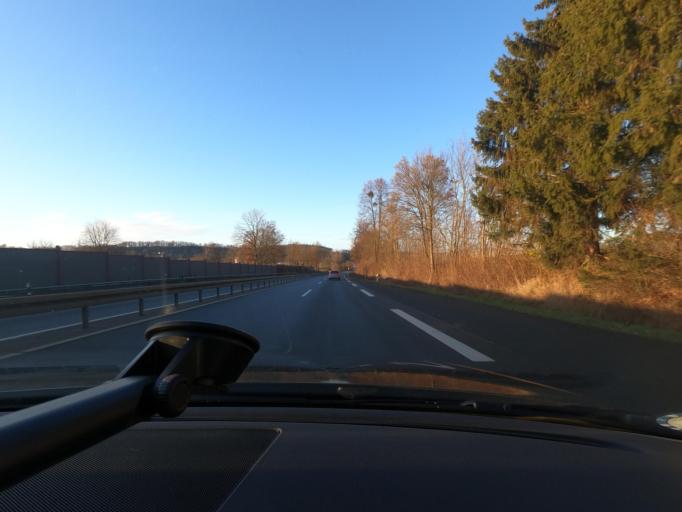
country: DE
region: Lower Saxony
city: Badenhausen
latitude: 51.7510
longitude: 10.2200
